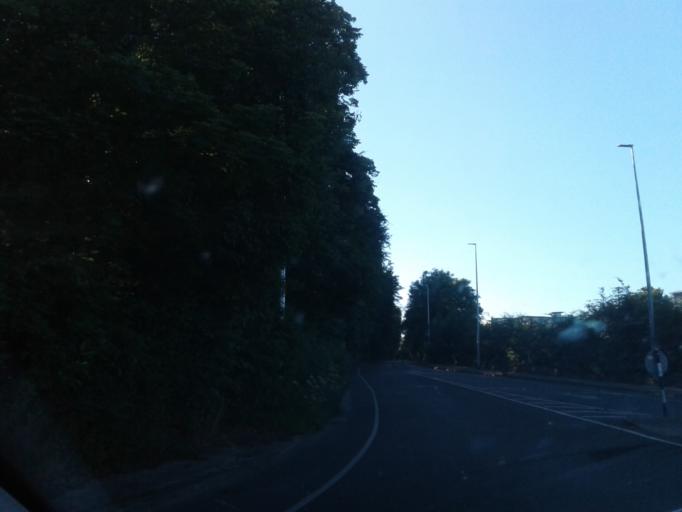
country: IE
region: Leinster
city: Sandyford
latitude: 53.2571
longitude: -6.2213
